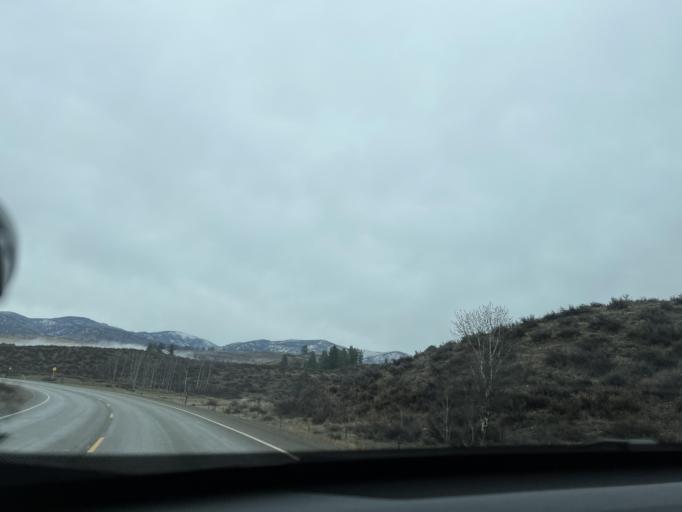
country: US
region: Washington
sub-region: Okanogan County
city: Brewster
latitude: 48.4697
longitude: -120.1995
